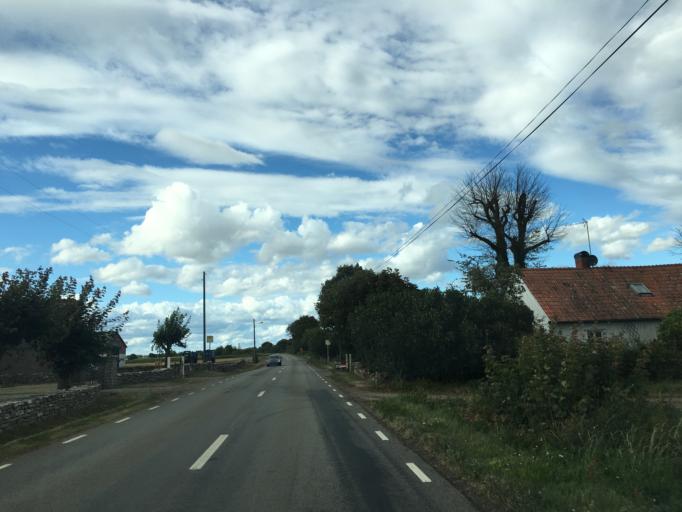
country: SE
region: Kalmar
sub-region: Morbylanga Kommun
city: Moerbylanga
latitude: 56.4202
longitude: 16.4354
